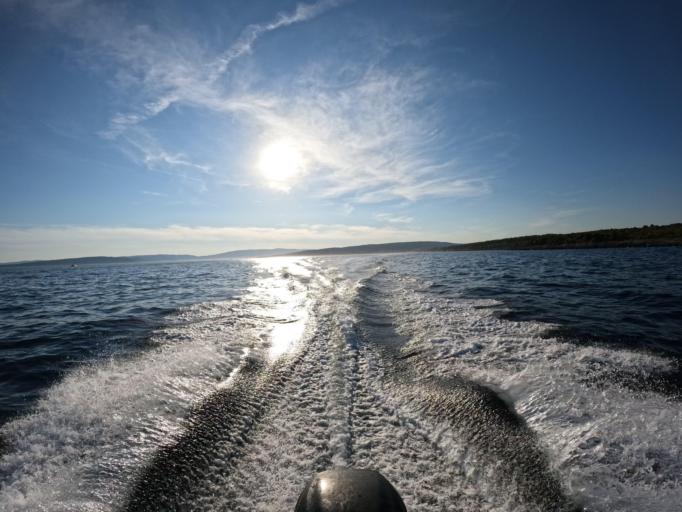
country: HR
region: Primorsko-Goranska
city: Punat
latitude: 45.0138
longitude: 14.6074
